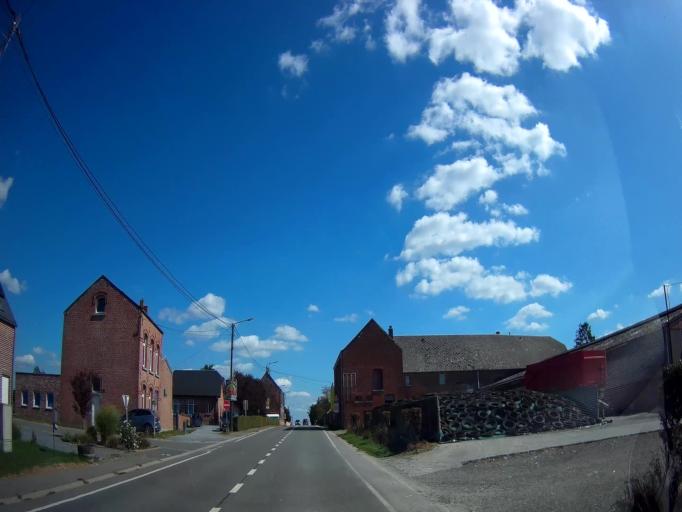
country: FR
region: Champagne-Ardenne
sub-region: Departement des Ardennes
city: Fromelennes
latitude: 50.1659
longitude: 4.8889
